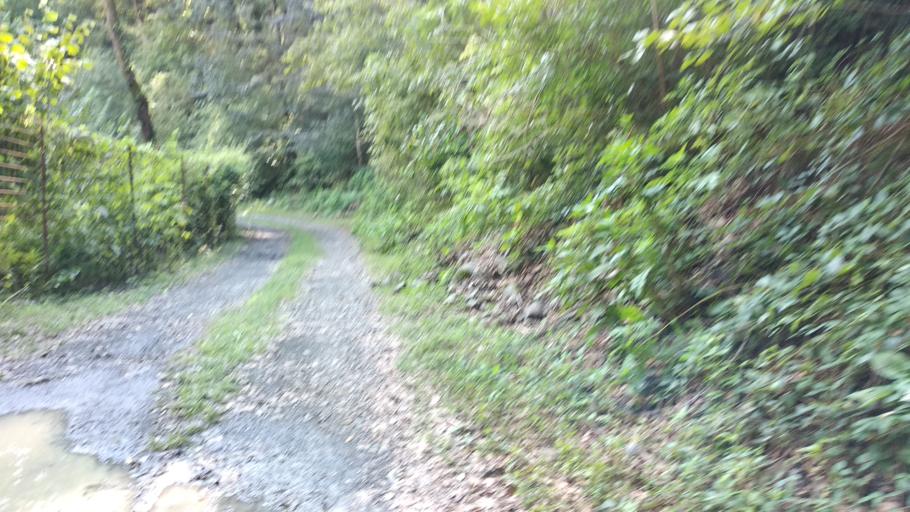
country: RU
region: Krasnodarskiy
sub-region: Sochi City
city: Sochi
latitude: 43.6355
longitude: 39.8213
